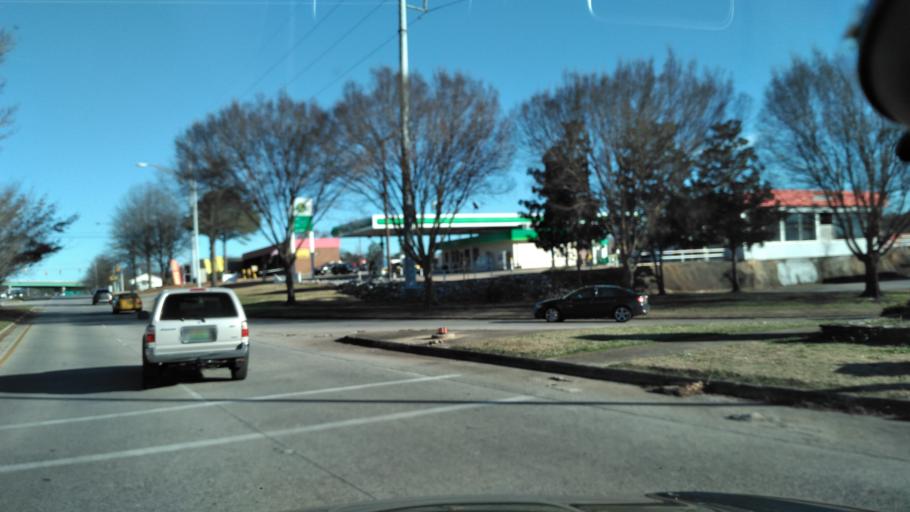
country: US
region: Alabama
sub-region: Jefferson County
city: Homewood
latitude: 33.4841
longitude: -86.7917
